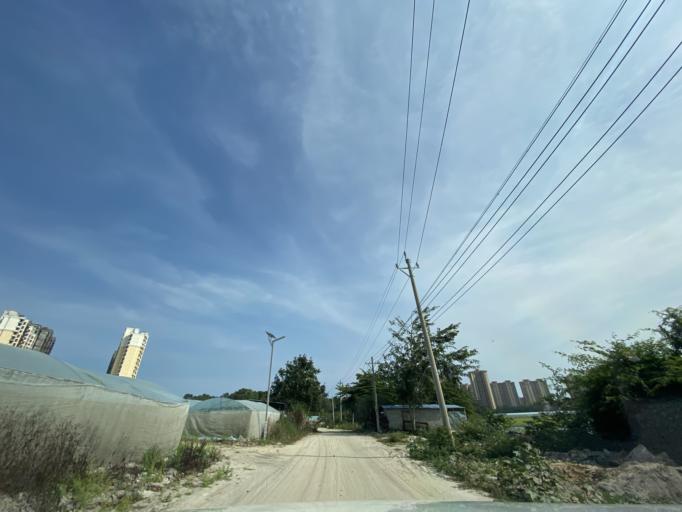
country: CN
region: Hainan
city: Yingzhou
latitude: 18.4056
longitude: 109.8372
